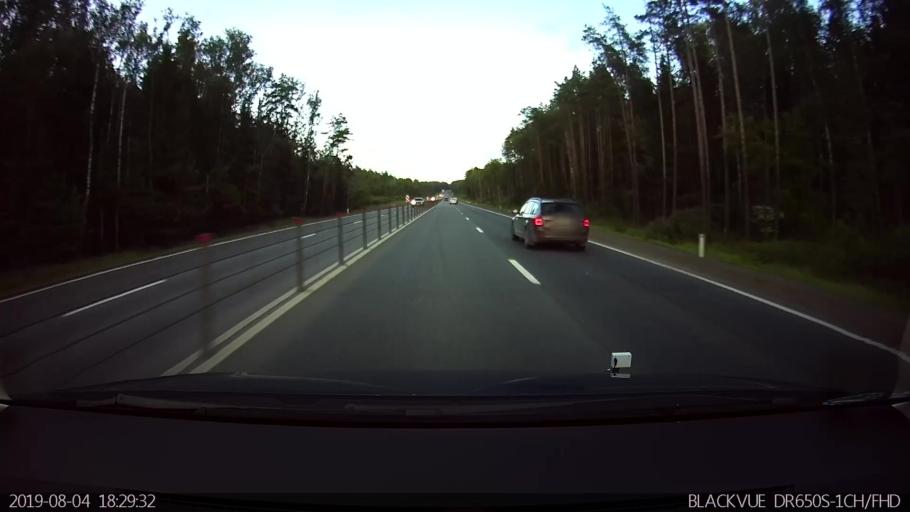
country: RU
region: Moskovskaya
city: Dorokhovo
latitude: 55.5449
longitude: 36.4346
